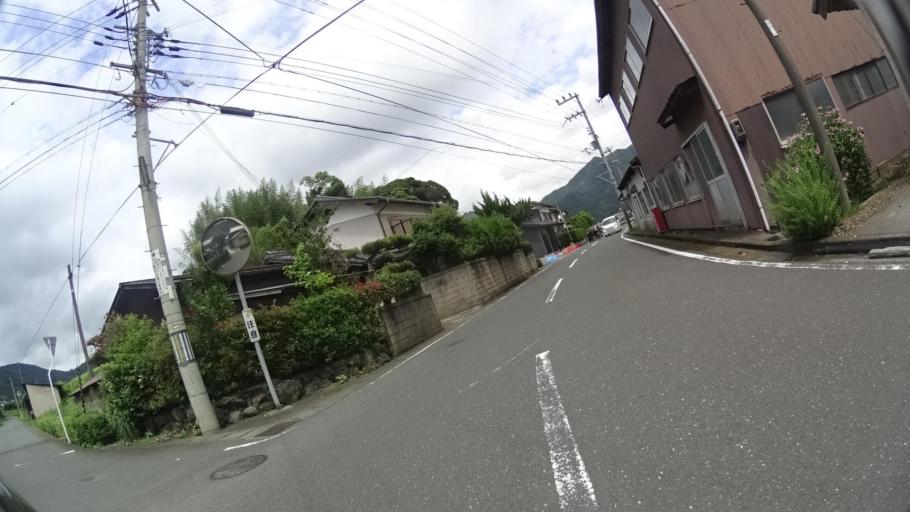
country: JP
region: Kyoto
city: Maizuru
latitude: 35.5166
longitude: 135.3891
